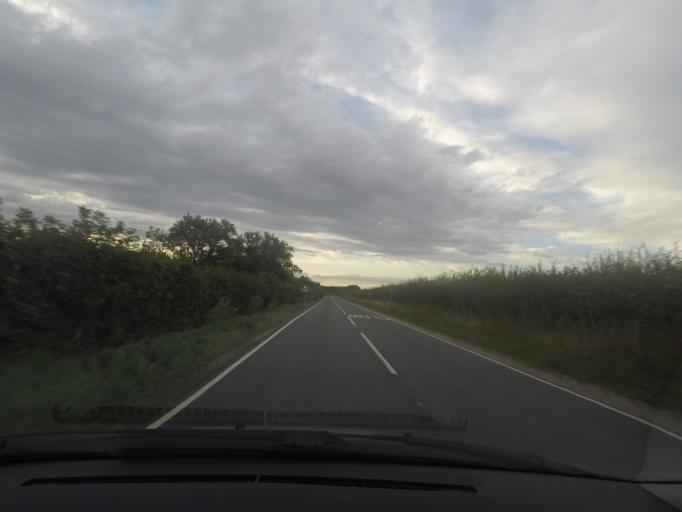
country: GB
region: England
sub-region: North East Lincolnshire
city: Wold Newton
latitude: 53.4378
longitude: -0.0709
